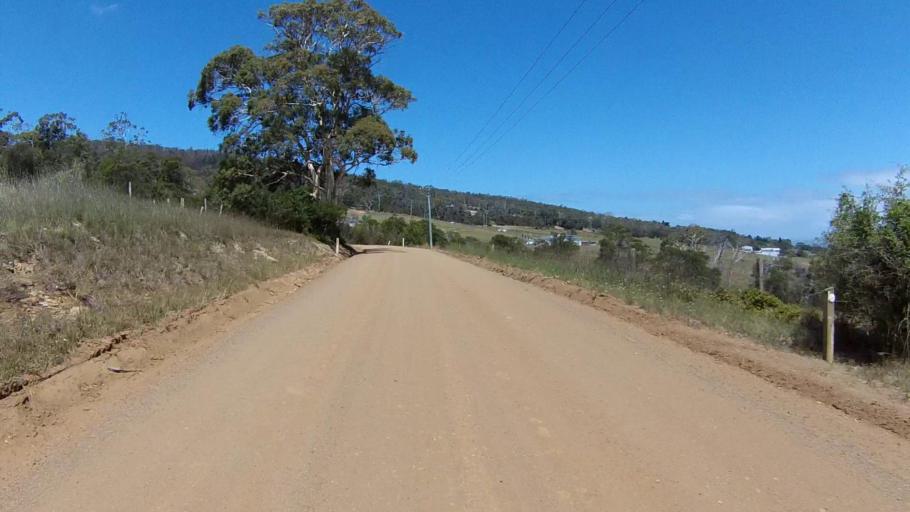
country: AU
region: Tasmania
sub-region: Clarence
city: Lauderdale
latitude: -42.9300
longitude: 147.4657
